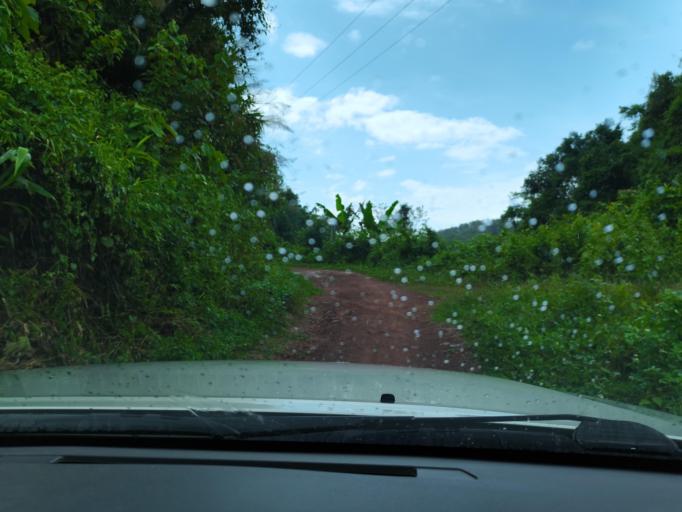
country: LA
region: Loungnamtha
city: Muang Nale
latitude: 20.5227
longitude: 101.0689
